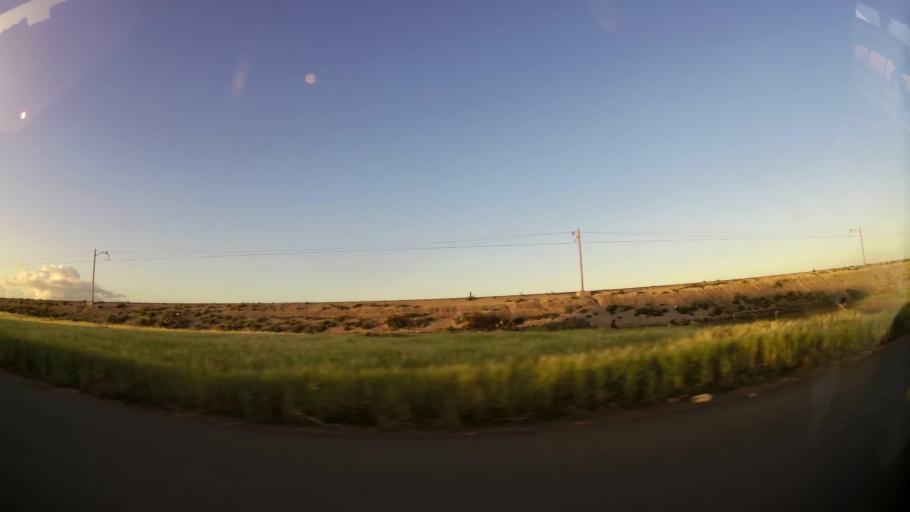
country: MA
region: Marrakech-Tensift-Al Haouz
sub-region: Kelaa-Des-Sraghna
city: Sidi Abdallah
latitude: 32.2397
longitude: -7.9302
